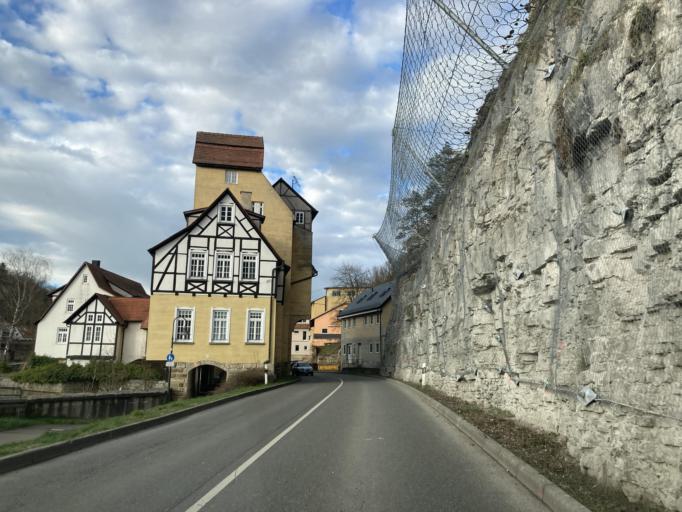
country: DE
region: Baden-Wuerttemberg
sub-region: Tuebingen Region
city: Rottenburg
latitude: 48.4667
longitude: 8.9214
